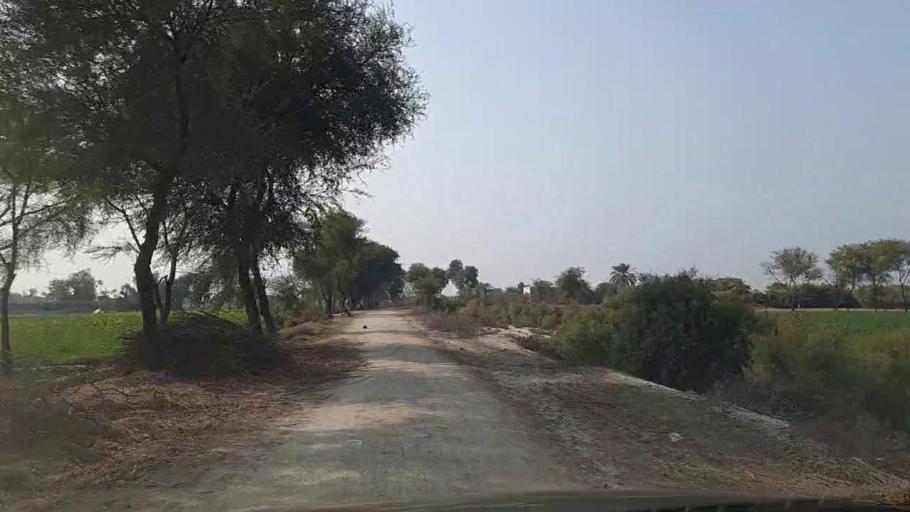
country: PK
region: Sindh
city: Daur
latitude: 26.3860
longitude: 68.3989
